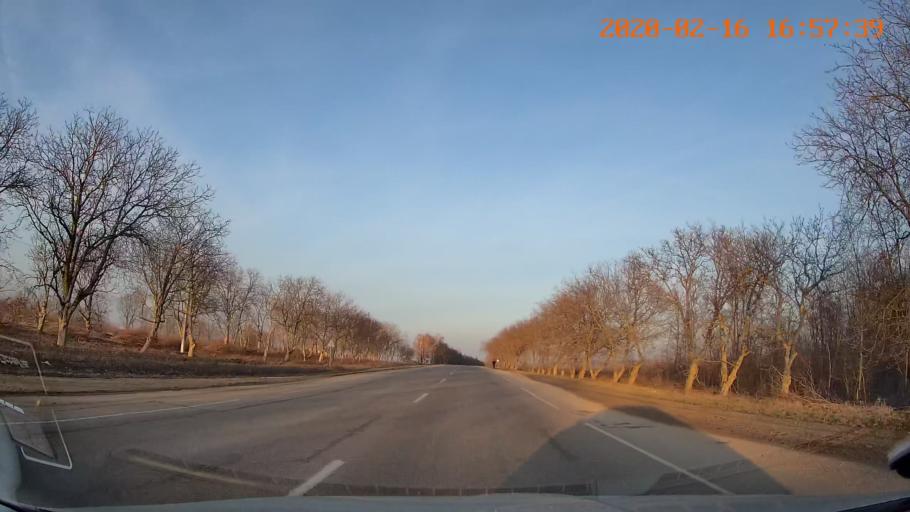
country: MD
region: Briceni
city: Briceni
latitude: 48.3446
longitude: 27.0712
